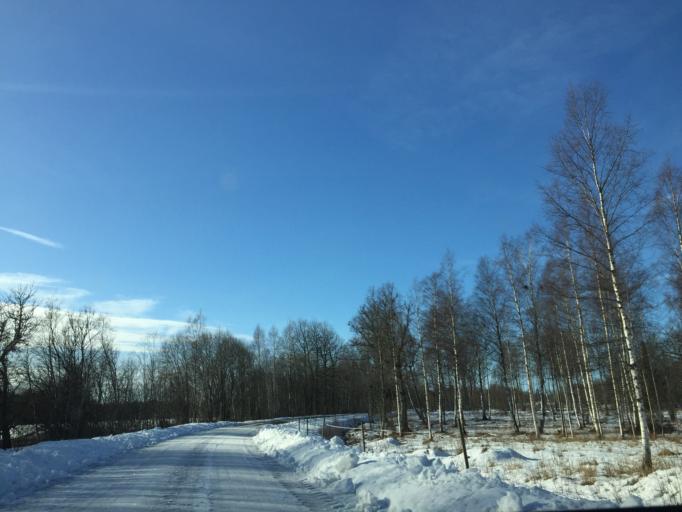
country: EE
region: Laeaene
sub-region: Lihula vald
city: Lihula
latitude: 58.6255
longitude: 23.6812
